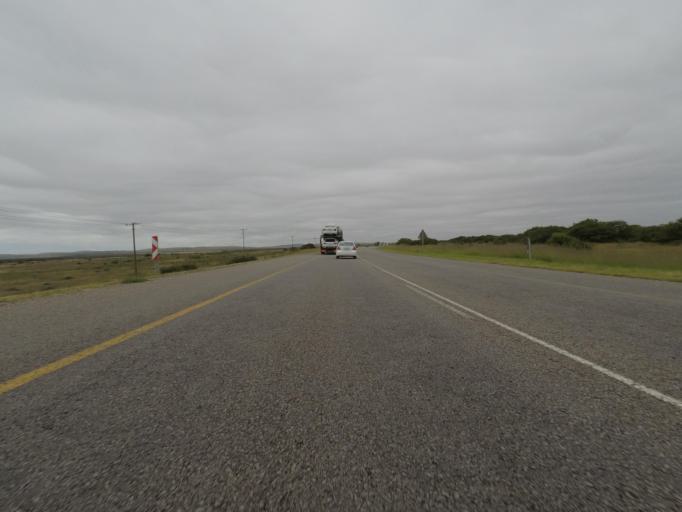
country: ZA
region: Eastern Cape
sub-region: Nelson Mandela Bay Metropolitan Municipality
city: Port Elizabeth
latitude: -33.6609
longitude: 25.8599
